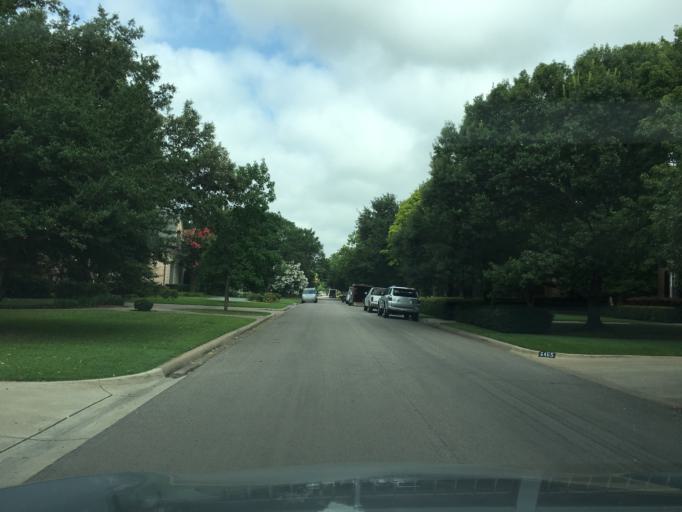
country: US
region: Texas
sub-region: Dallas County
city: University Park
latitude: 32.8822
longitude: -96.7937
